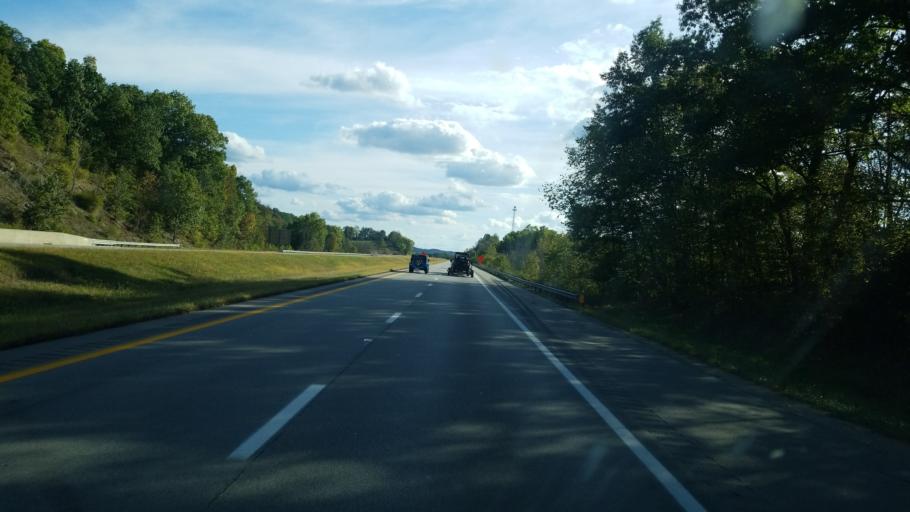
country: US
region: Ohio
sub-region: Guernsey County
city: Byesville
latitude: 39.9526
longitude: -81.5323
